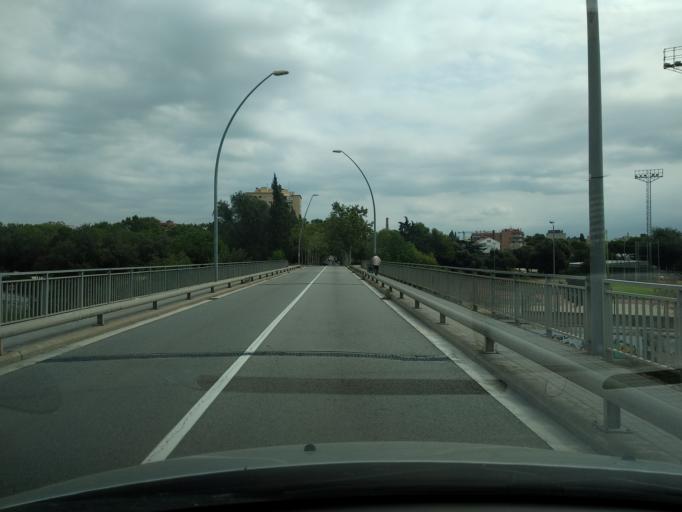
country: ES
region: Catalonia
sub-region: Provincia de Barcelona
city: Granollers
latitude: 41.6018
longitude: 2.2791
